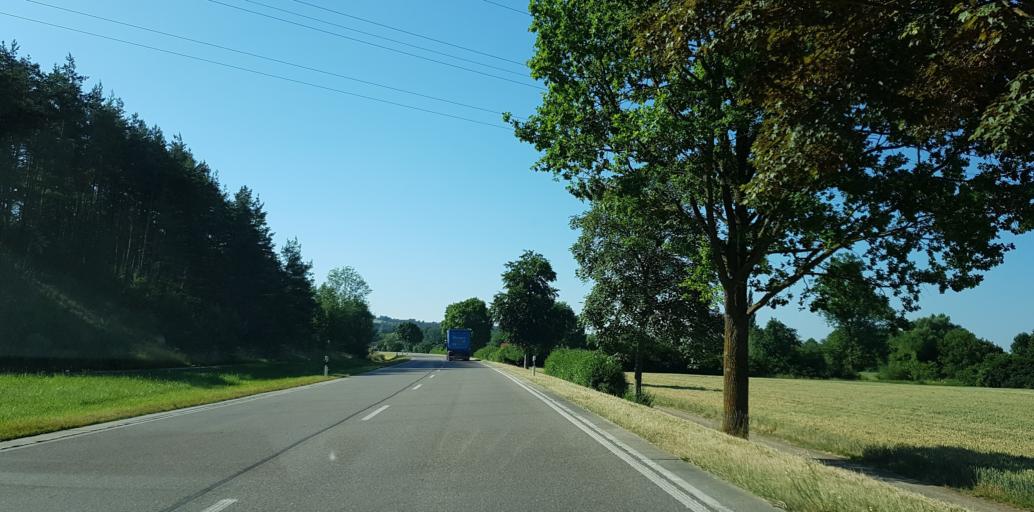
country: DE
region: Baden-Wuerttemberg
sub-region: Tuebingen Region
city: Allmendingen
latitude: 48.3398
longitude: 9.7217
